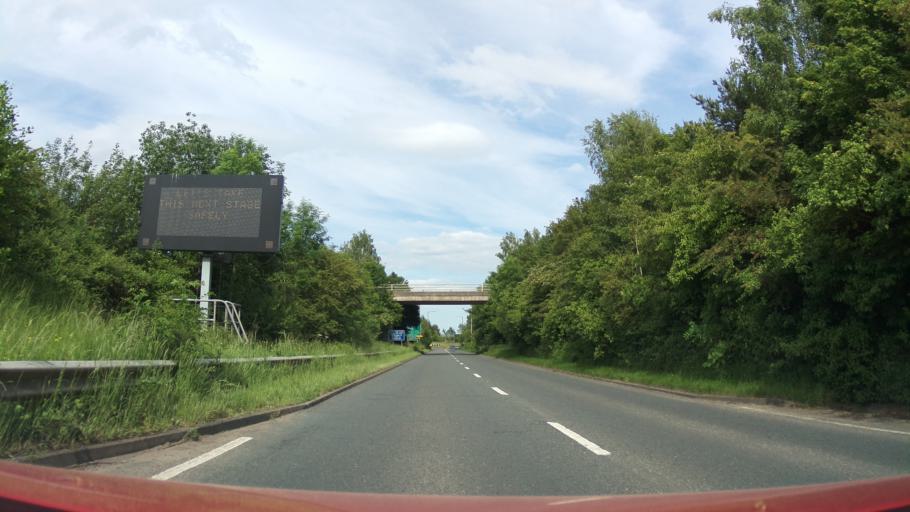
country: GB
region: England
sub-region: Worcestershire
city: Bransford
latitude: 52.1871
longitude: -2.2703
